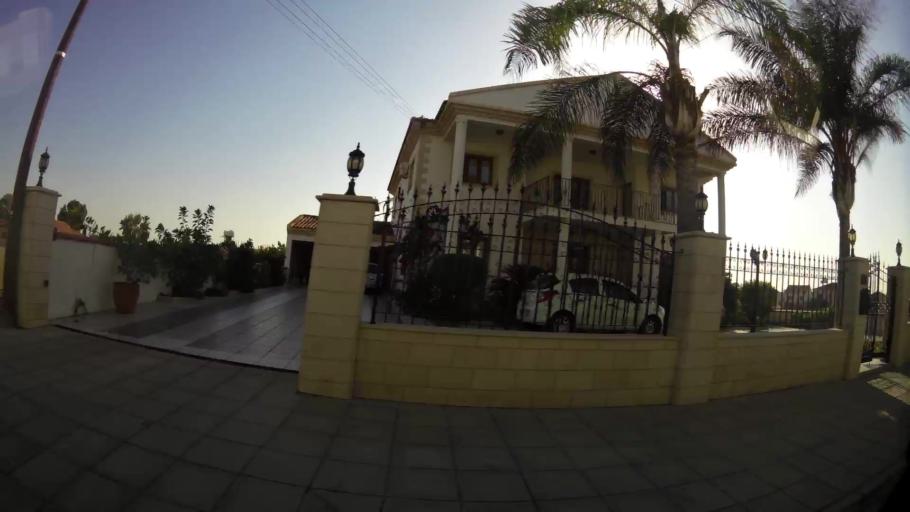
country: CY
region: Larnaka
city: Aradippou
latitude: 34.9417
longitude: 33.5958
